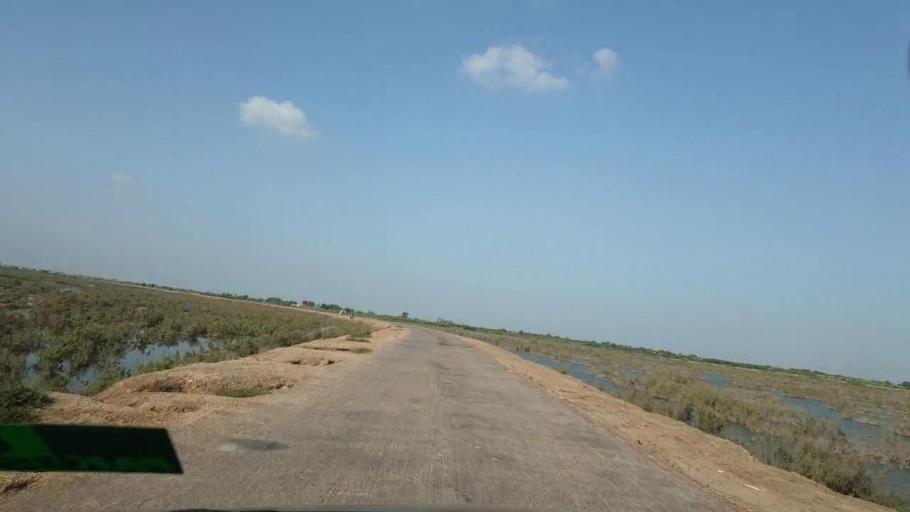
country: PK
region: Sindh
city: Tando Bago
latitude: 24.7273
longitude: 69.1980
